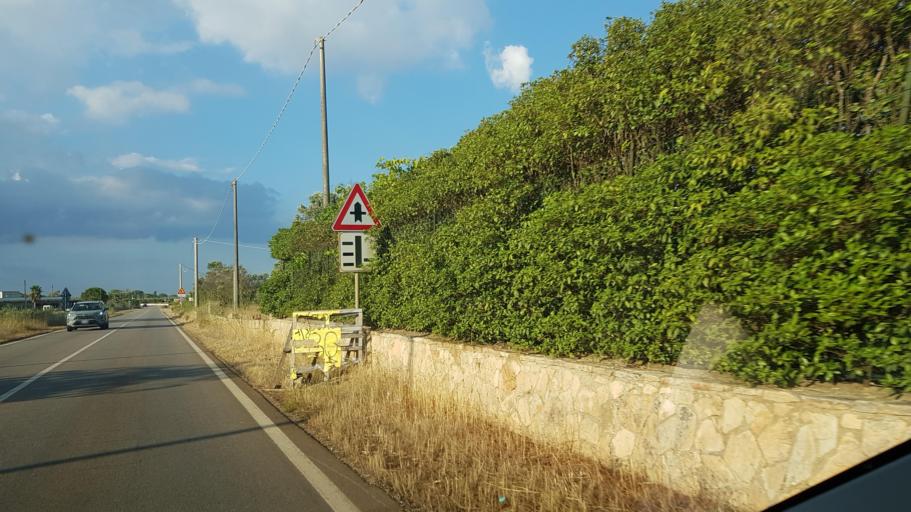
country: IT
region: Apulia
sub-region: Provincia di Lecce
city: Acquarica del Capo
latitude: 39.8707
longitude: 18.2209
